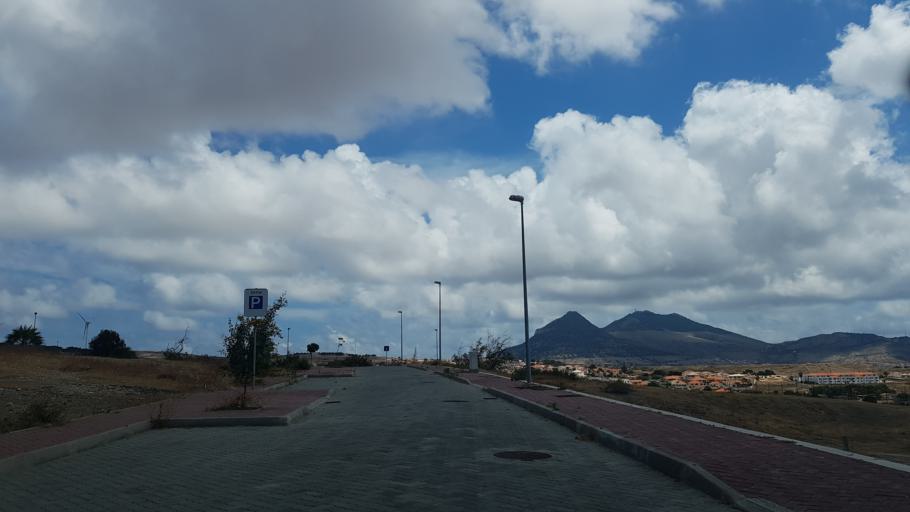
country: PT
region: Madeira
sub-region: Porto Santo
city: Vila de Porto Santo
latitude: 33.0491
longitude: -16.3620
